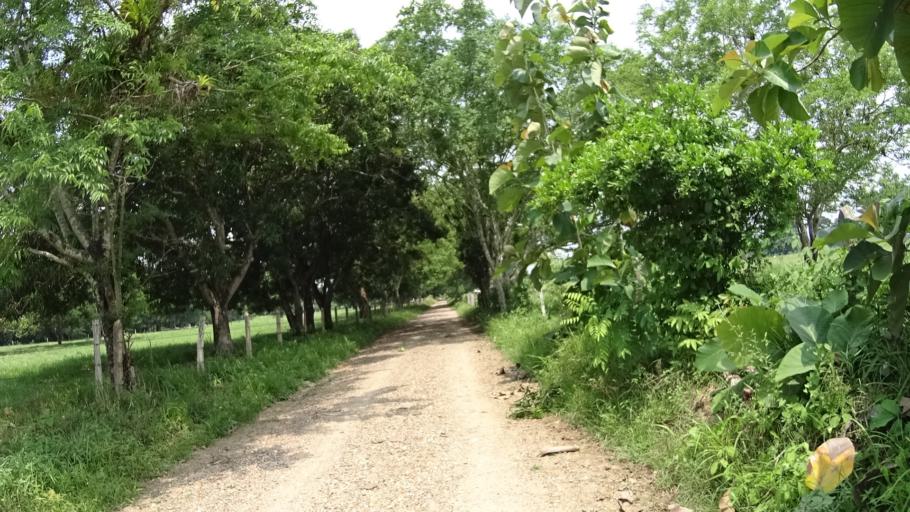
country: CO
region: Cundinamarca
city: Puerto Salgar
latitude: 5.5420
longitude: -74.6701
